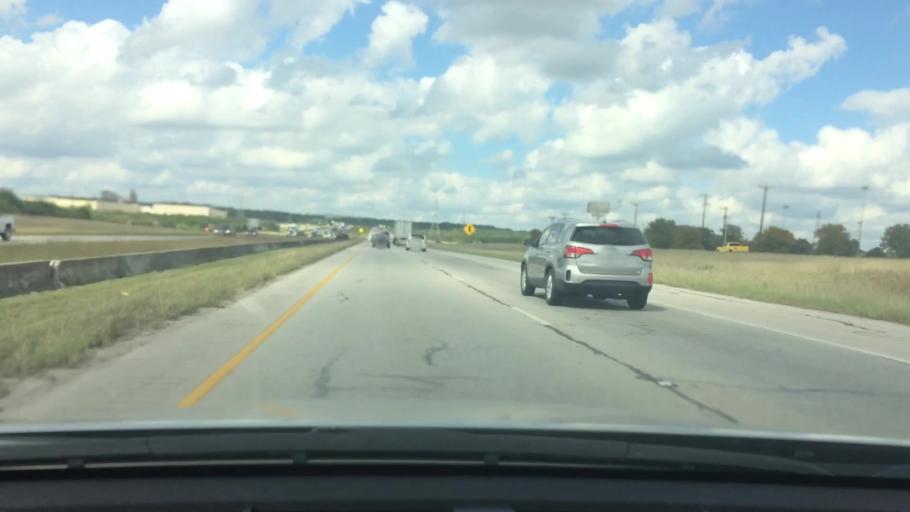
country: US
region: Texas
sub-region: Bexar County
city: Live Oak
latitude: 29.5947
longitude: -98.3538
